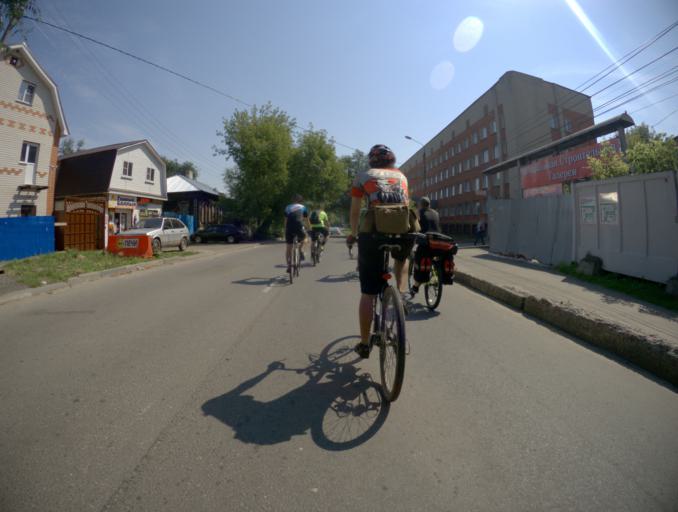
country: RU
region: Nizjnij Novgorod
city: Nizhniy Novgorod
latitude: 56.3166
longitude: 43.9495
